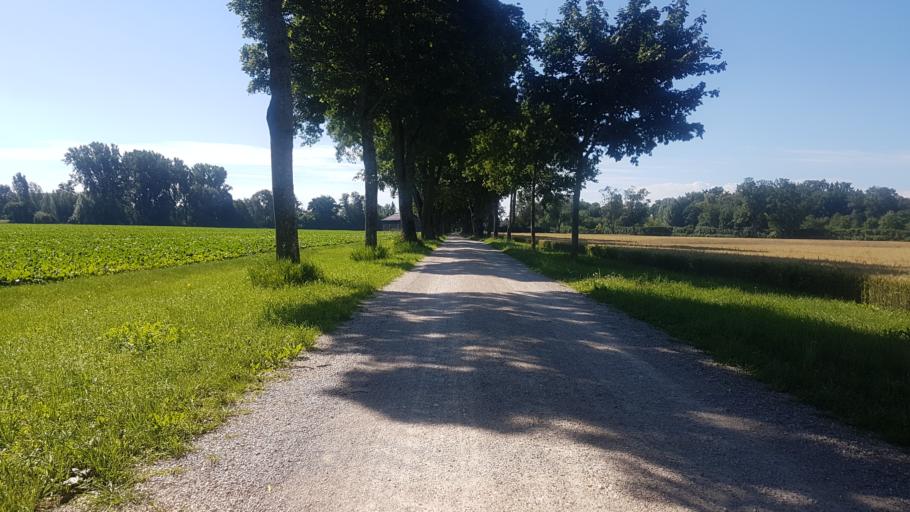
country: DE
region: Bavaria
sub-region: Upper Bavaria
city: Bergheim
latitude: 48.7309
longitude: 11.2697
